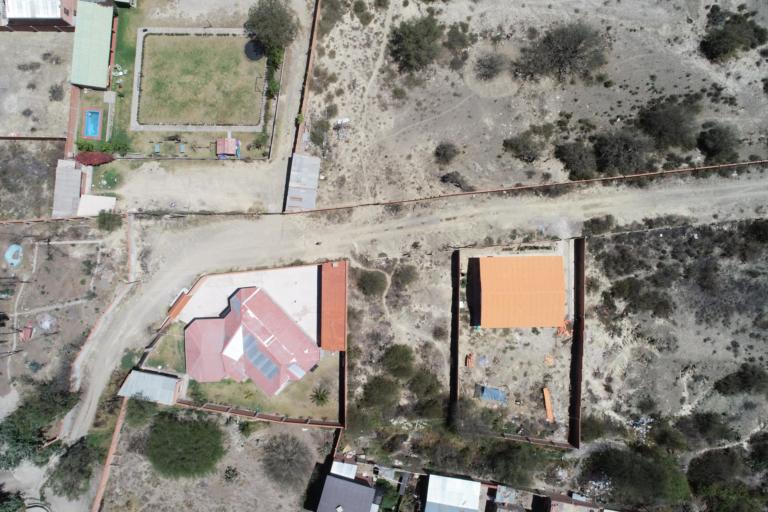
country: BO
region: La Paz
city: La Paz
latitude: -16.6272
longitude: -68.0542
